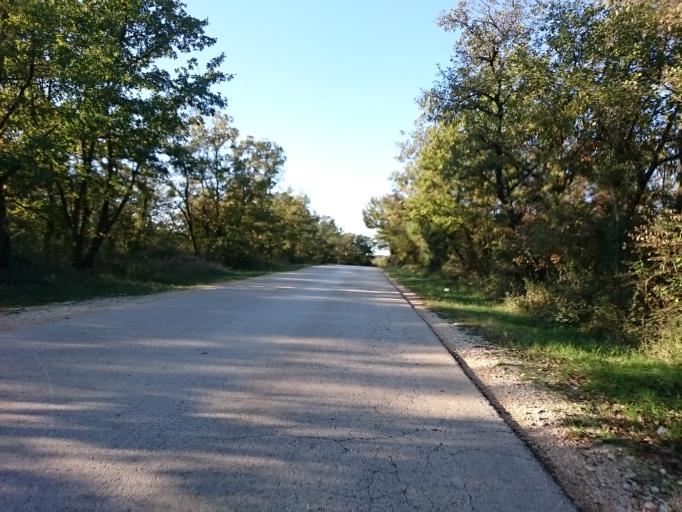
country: HR
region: Istarska
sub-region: Grad Porec
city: Porec
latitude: 45.2838
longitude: 13.6441
